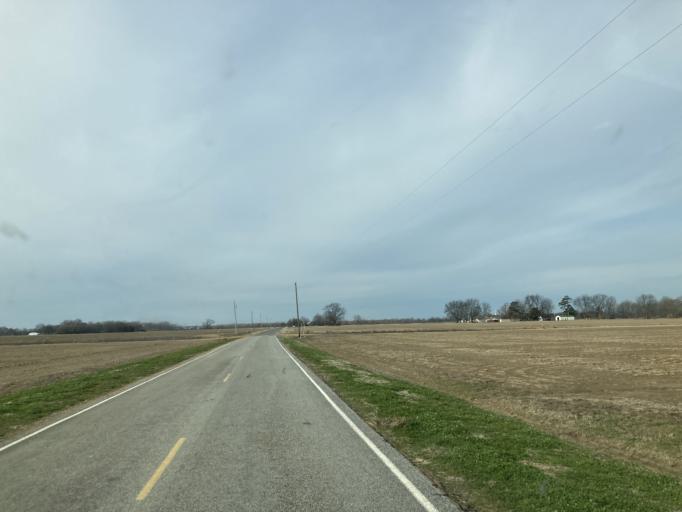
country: US
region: Mississippi
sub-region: Humphreys County
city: Belzoni
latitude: 33.0564
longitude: -90.6562
